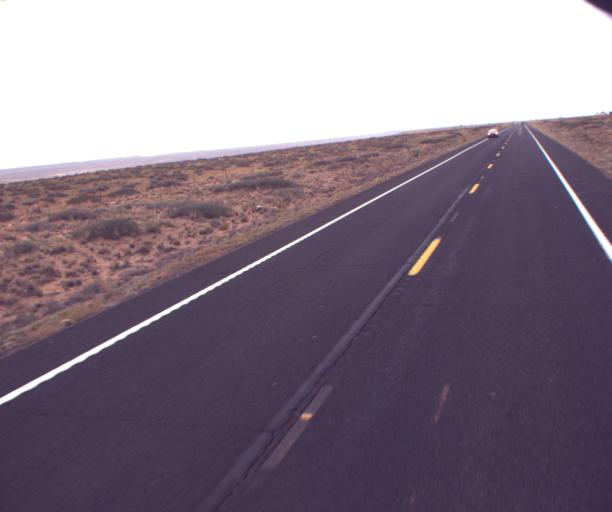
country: US
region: Arizona
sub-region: Coconino County
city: Tuba City
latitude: 36.1582
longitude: -111.1132
